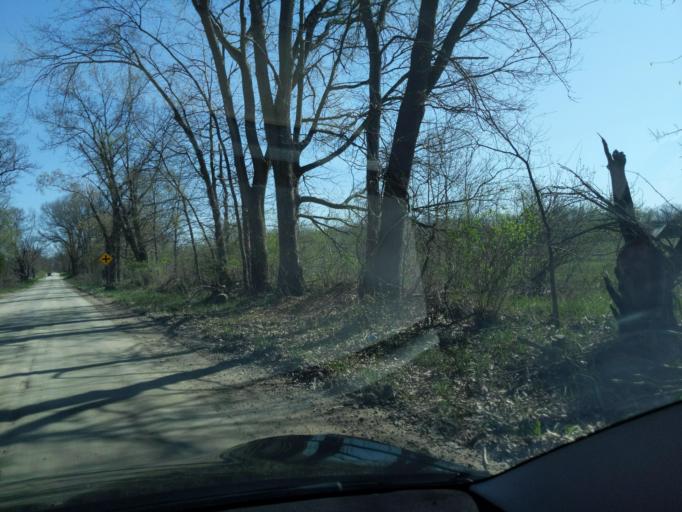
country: US
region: Michigan
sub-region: Ingham County
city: Stockbridge
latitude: 42.4091
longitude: -84.0837
